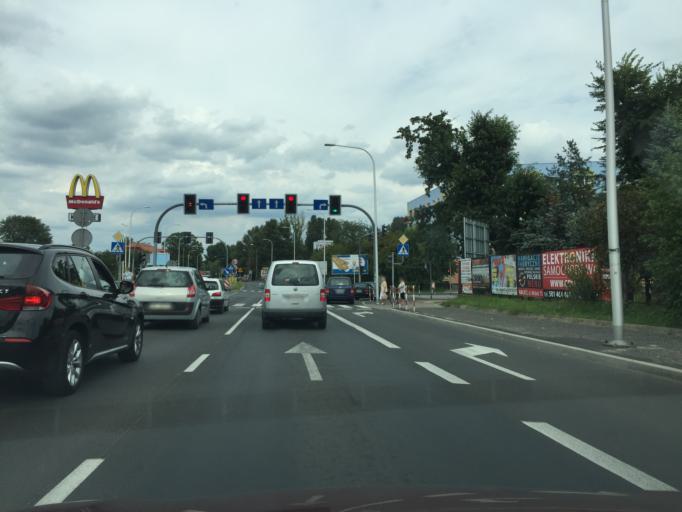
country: PL
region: Greater Poland Voivodeship
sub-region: Kalisz
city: Kalisz
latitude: 51.7618
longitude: 18.0783
